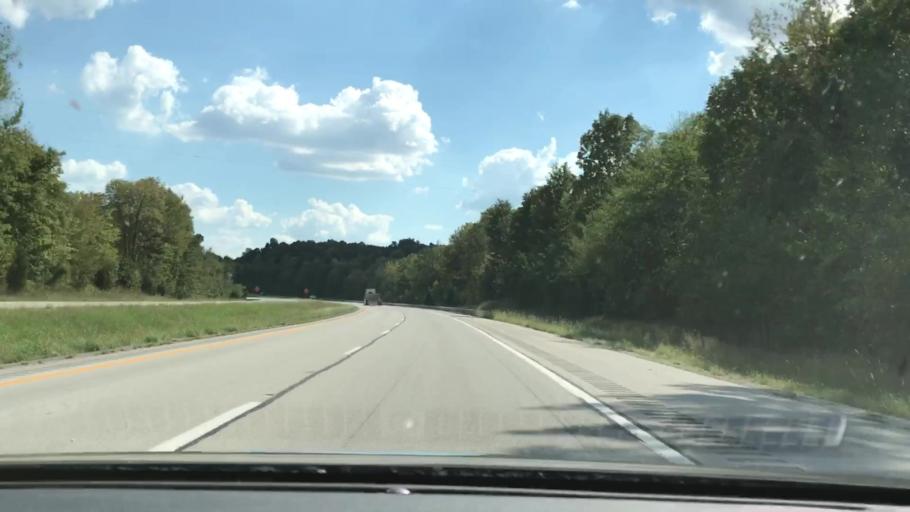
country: US
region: Kentucky
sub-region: Butler County
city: Morgantown
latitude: 37.2646
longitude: -86.7485
